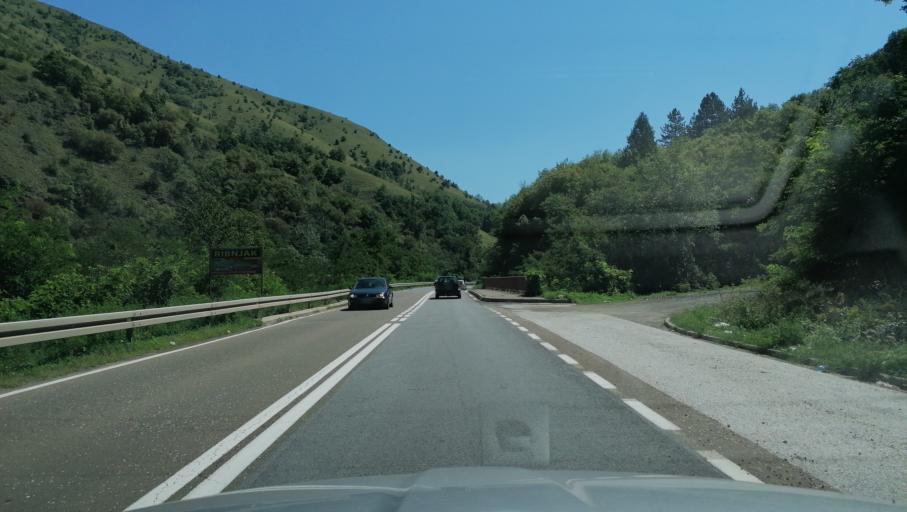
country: RS
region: Central Serbia
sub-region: Raski Okrug
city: Kraljevo
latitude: 43.5748
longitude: 20.5909
